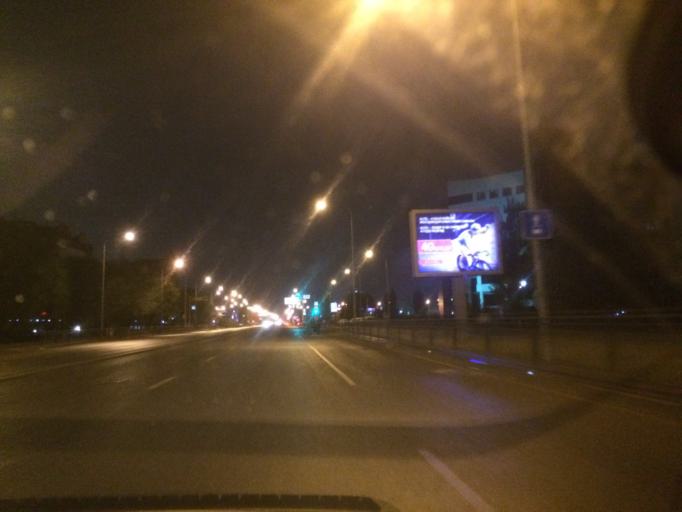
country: KZ
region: Astana Qalasy
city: Astana
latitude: 51.1556
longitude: 71.4716
